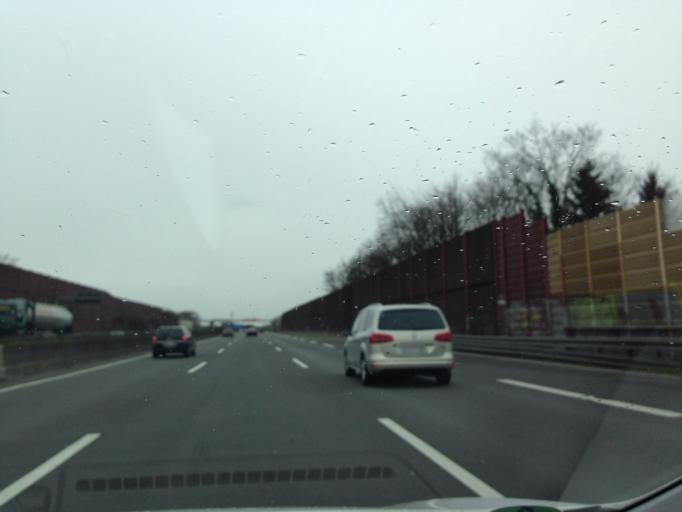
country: DE
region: North Rhine-Westphalia
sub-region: Regierungsbezirk Dusseldorf
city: Meerbusch
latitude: 51.2667
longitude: 6.6438
